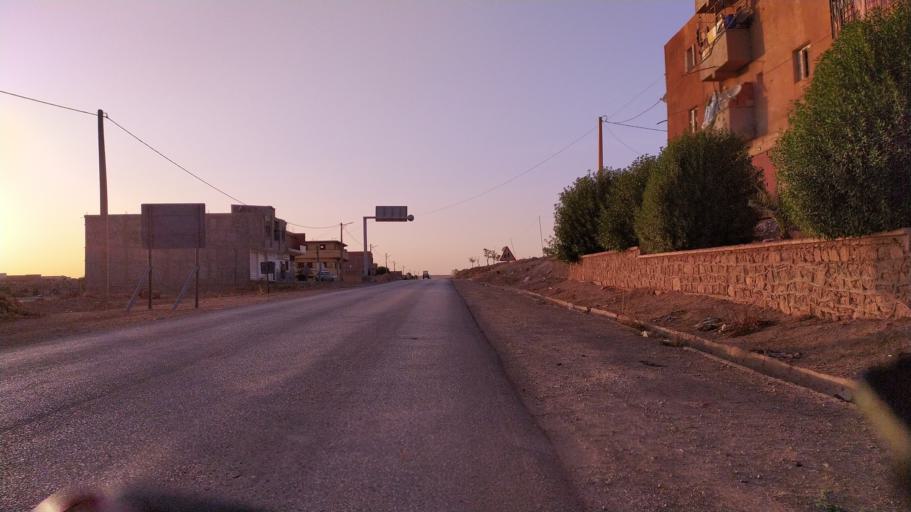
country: DZ
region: Tiaret
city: Frenda
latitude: 34.8979
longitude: 1.2473
